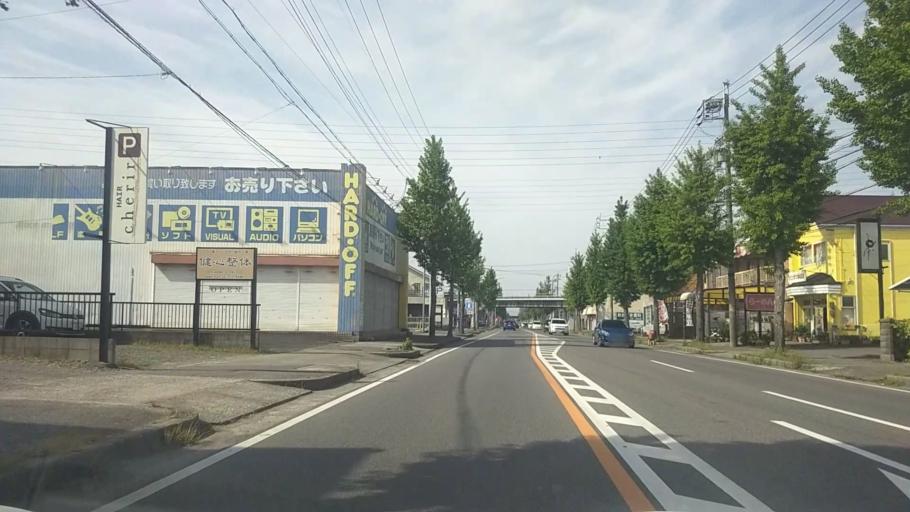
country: JP
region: Aichi
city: Okazaki
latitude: 34.9432
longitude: 137.1529
